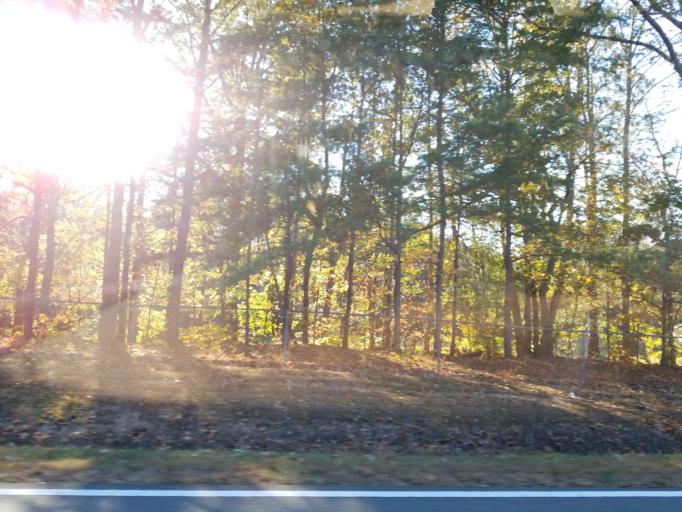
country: US
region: Georgia
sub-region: Pickens County
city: Jasper
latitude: 34.5523
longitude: -84.4691
